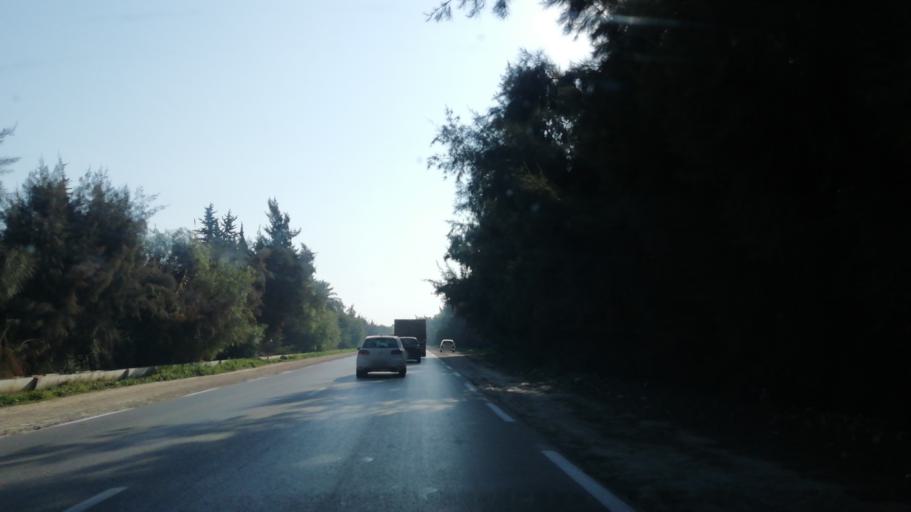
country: DZ
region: Relizane
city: Relizane
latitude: 35.7308
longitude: 0.4728
